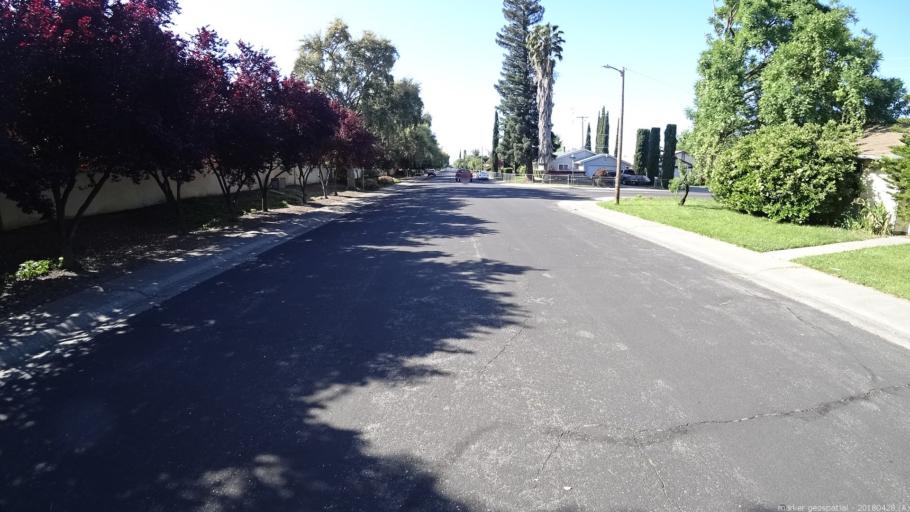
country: US
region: California
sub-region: Yolo County
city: West Sacramento
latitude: 38.6001
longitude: -121.5263
